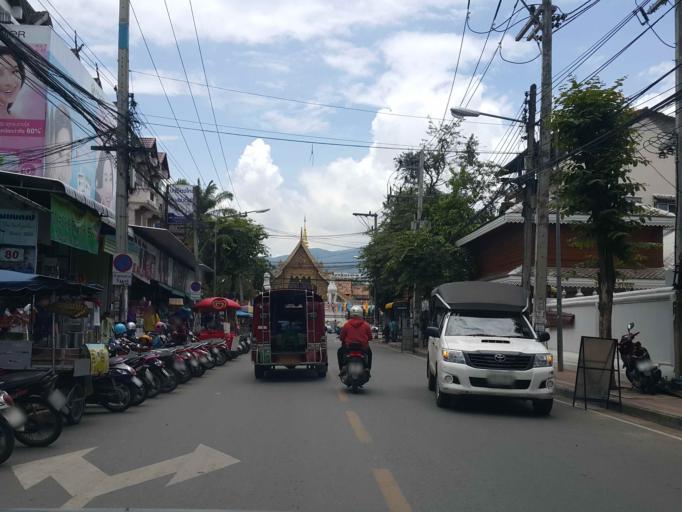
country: TH
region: Chiang Mai
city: Chiang Mai
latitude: 18.7885
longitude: 98.9833
